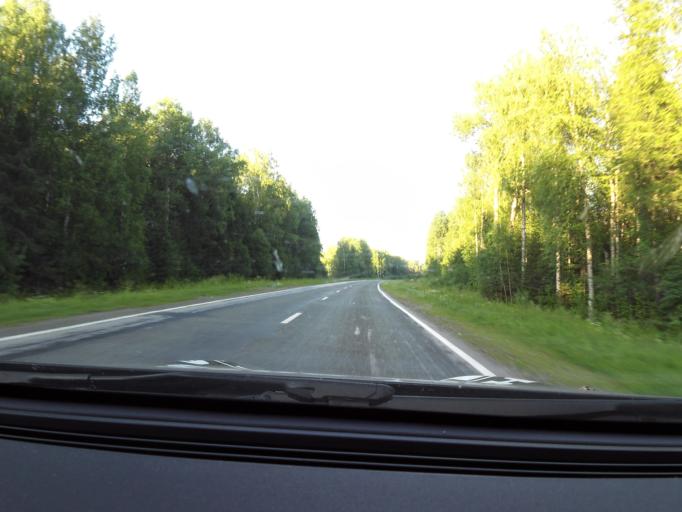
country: RU
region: Perm
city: Siva
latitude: 58.6415
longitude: 53.8235
